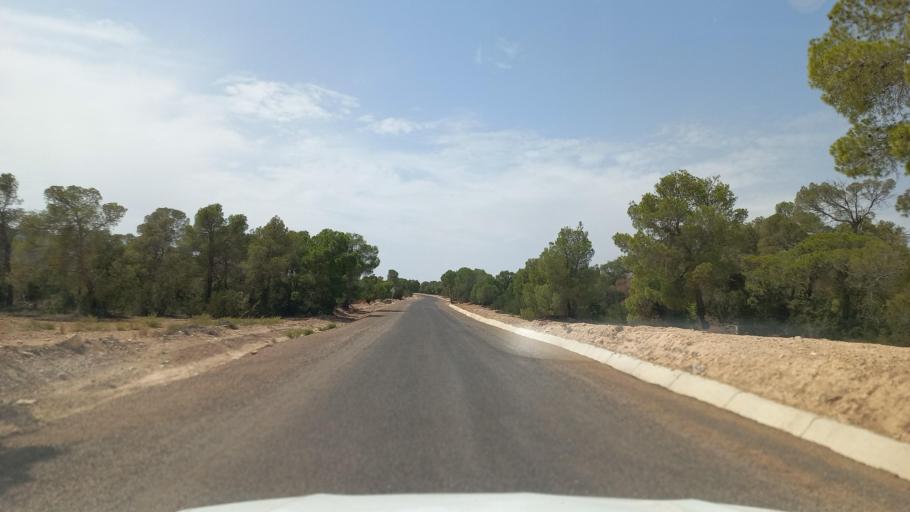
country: TN
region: Al Qasrayn
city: Sbiba
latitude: 35.3828
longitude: 8.9300
